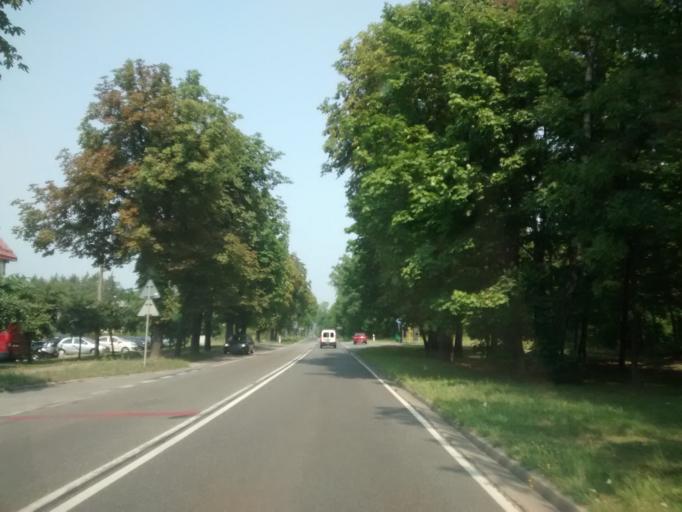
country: PL
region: Lesser Poland Voivodeship
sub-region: Powiat olkuski
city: Klucze
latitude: 50.3412
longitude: 19.5624
